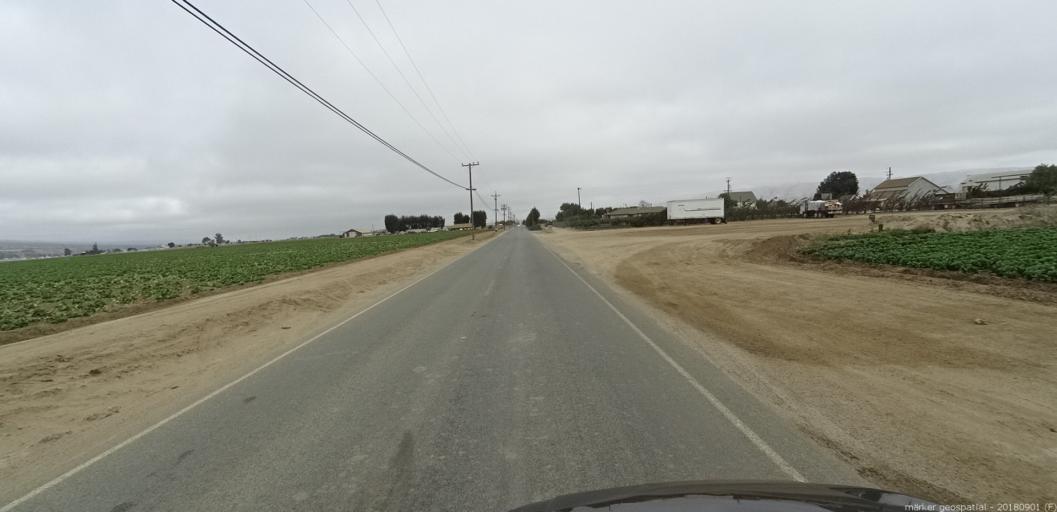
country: US
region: California
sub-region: Monterey County
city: Soledad
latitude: 36.3807
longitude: -121.3288
